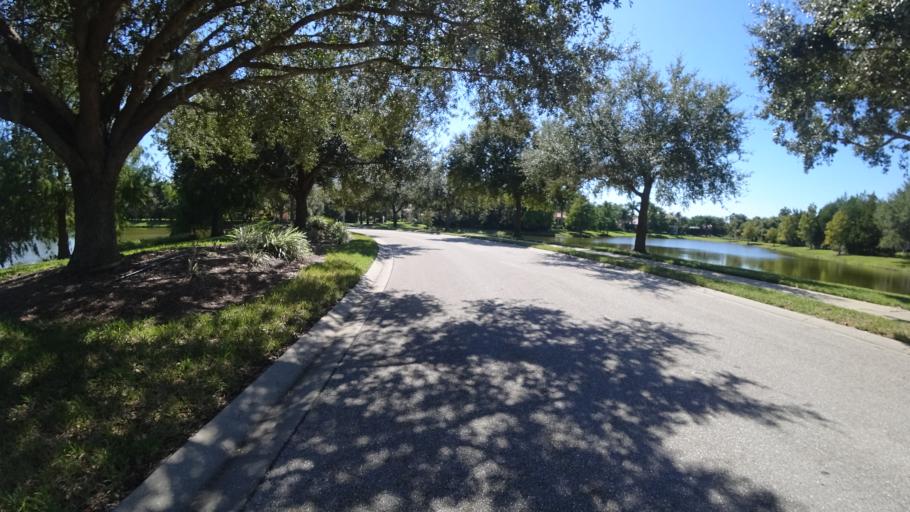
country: US
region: Florida
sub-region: Sarasota County
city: The Meadows
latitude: 27.4127
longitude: -82.4063
